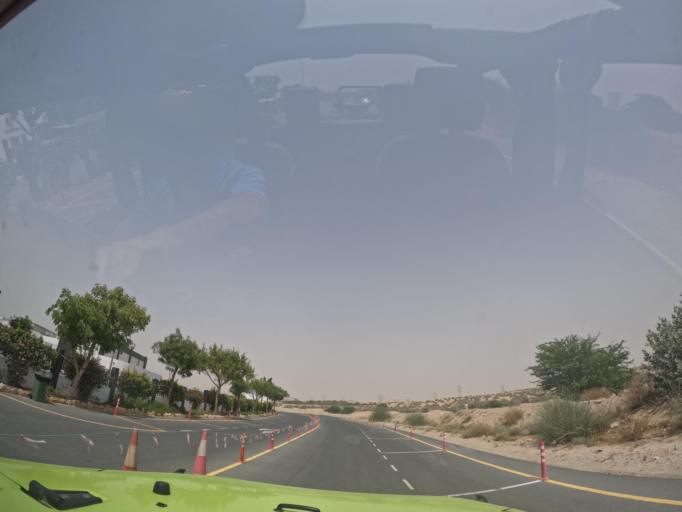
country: AE
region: Ash Shariqah
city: Sharjah
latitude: 25.1046
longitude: 55.4024
